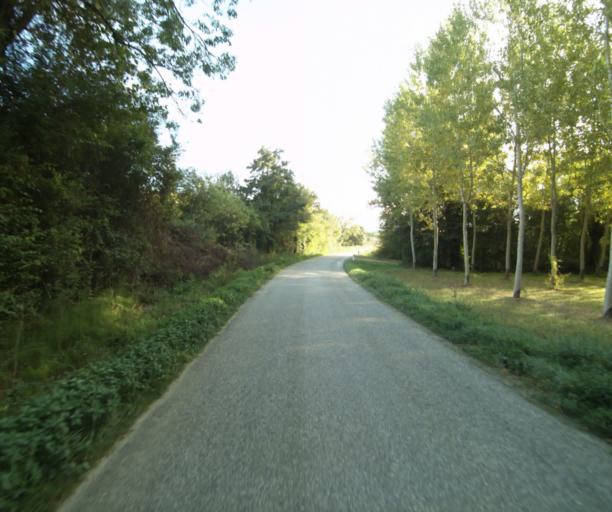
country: FR
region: Midi-Pyrenees
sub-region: Departement du Gers
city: Gondrin
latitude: 43.8903
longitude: 0.2985
